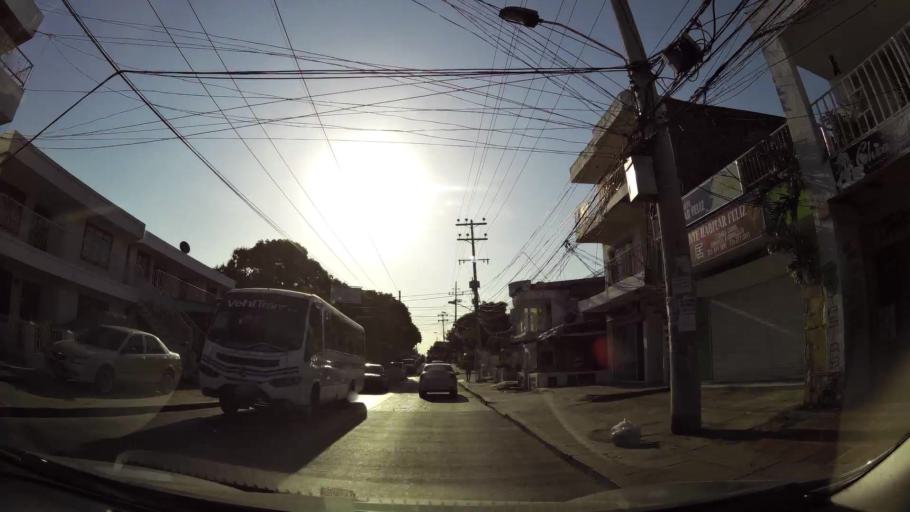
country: CO
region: Bolivar
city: Cartagena
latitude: 10.4013
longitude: -75.5029
